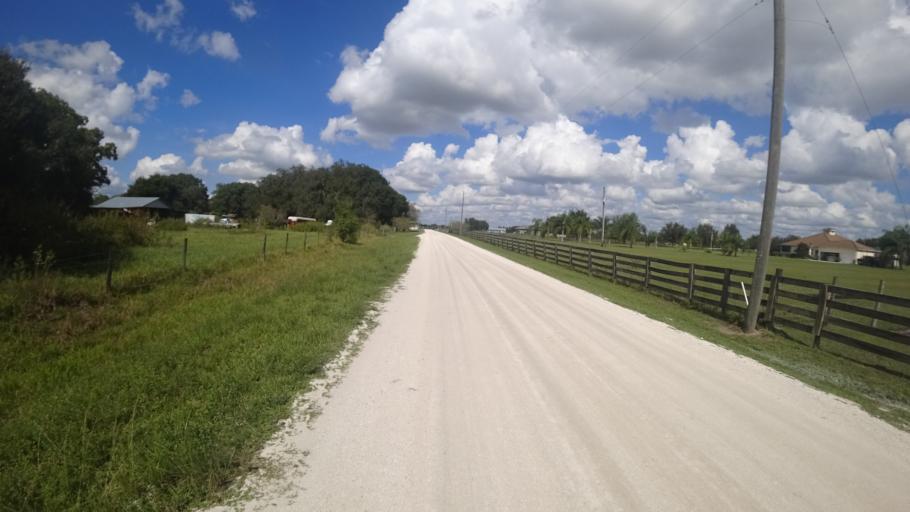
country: US
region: Florida
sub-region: Sarasota County
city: Warm Mineral Springs
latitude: 27.2702
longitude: -82.1544
